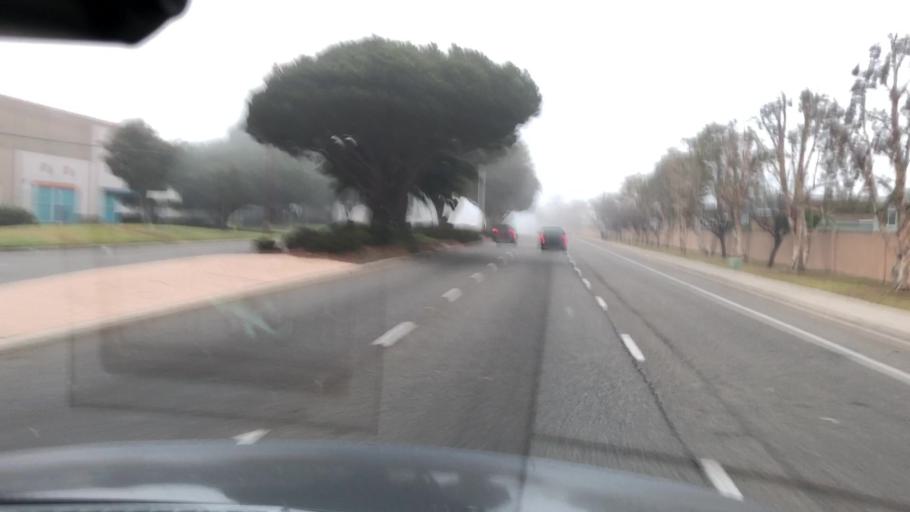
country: US
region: California
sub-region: Ventura County
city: Oxnard
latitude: 34.1801
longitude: -119.1598
